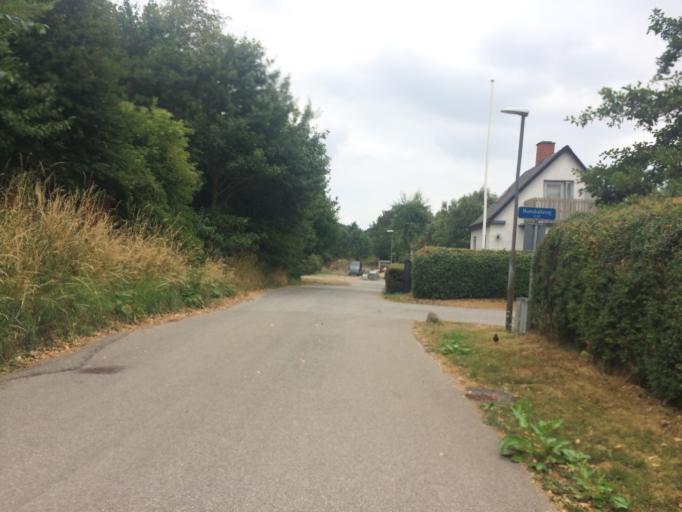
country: DK
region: Central Jutland
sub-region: Struer Kommune
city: Struer
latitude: 56.4823
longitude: 8.6103
